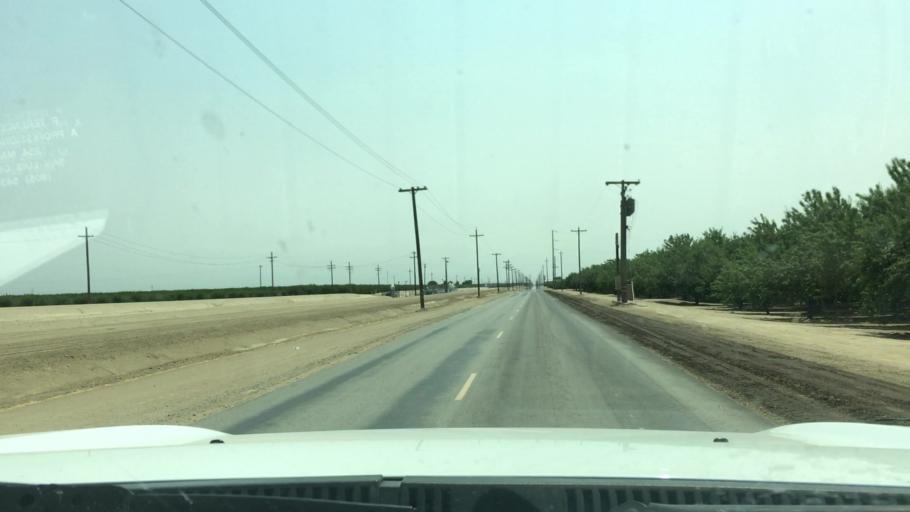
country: US
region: California
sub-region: Kern County
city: Wasco
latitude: 35.6188
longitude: -119.4379
